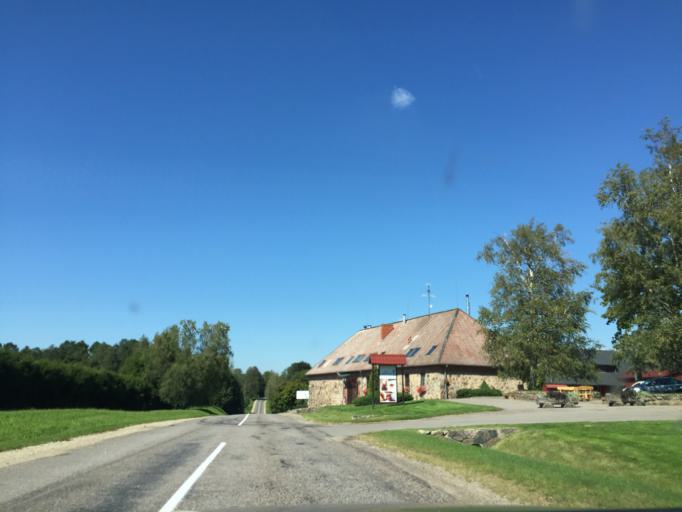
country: LV
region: Limbazu Rajons
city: Limbazi
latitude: 57.4861
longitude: 24.7103
